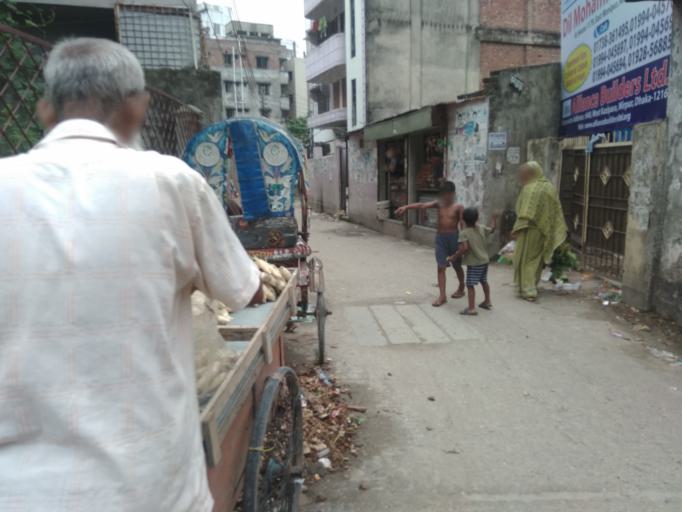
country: BD
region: Dhaka
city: Azimpur
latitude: 23.8013
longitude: 90.3689
